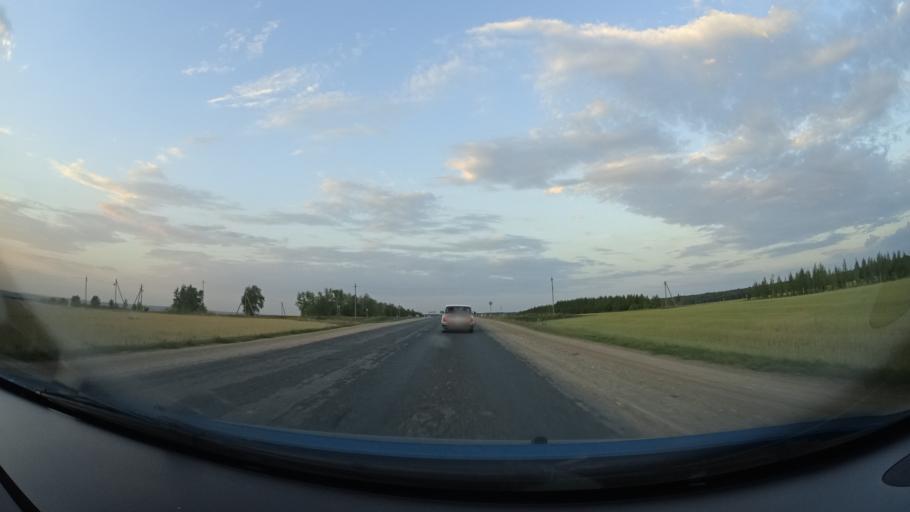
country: RU
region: Tatarstan
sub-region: Bugul'minskiy Rayon
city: Bugul'ma
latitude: 54.2428
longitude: 52.8043
